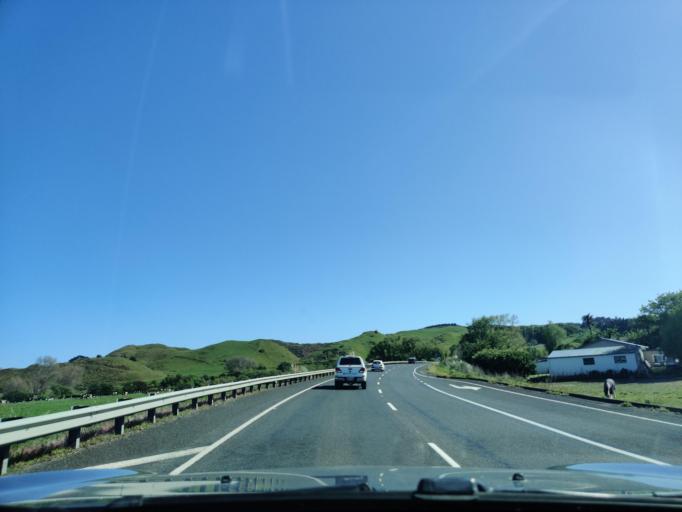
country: NZ
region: Manawatu-Wanganui
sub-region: Wanganui District
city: Wanganui
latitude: -40.0078
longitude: 175.1678
